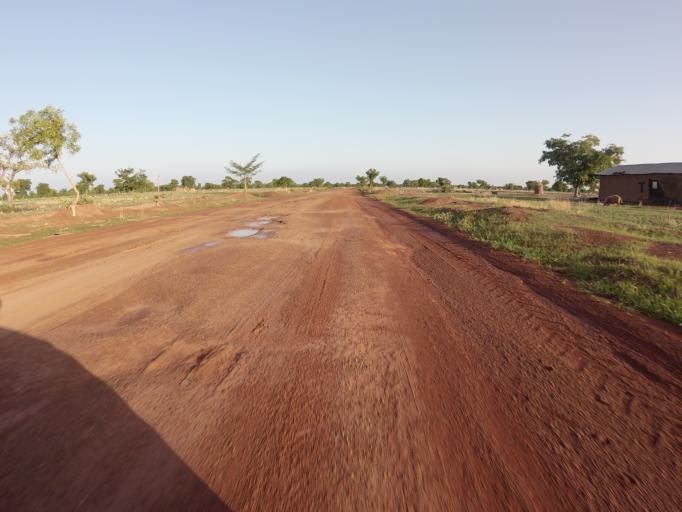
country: TG
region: Savanes
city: Sansanne-Mango
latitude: 10.2948
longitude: -0.0881
